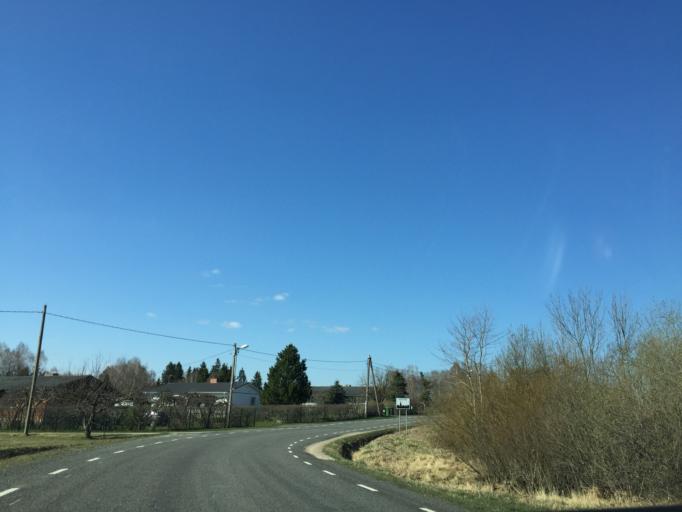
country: EE
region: Viljandimaa
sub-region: Viiratsi vald
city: Viiratsi
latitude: 58.2751
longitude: 25.6855
